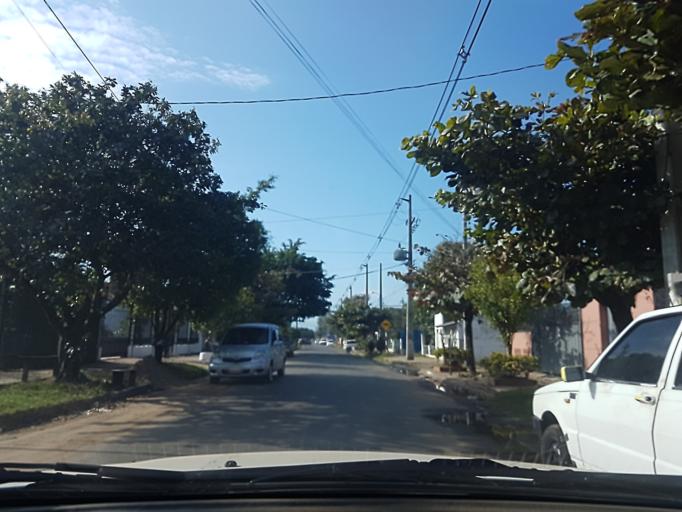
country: PY
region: Central
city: Colonia Mariano Roque Alonso
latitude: -25.2497
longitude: -57.5355
